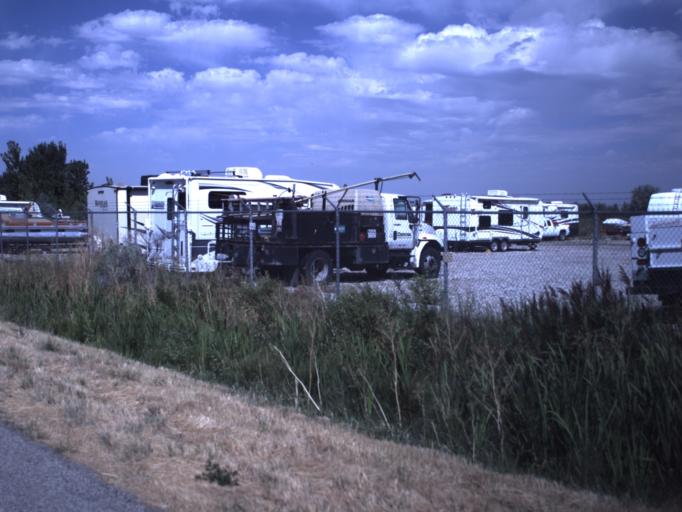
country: US
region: Utah
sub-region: Box Elder County
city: Willard
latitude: 41.4226
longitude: -112.0439
